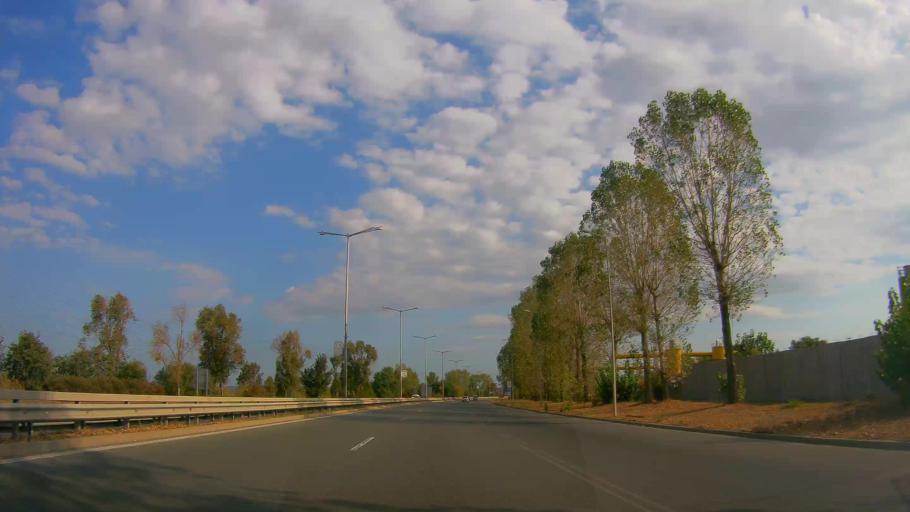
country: BG
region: Burgas
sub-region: Obshtina Burgas
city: Burgas
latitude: 42.4779
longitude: 27.4360
